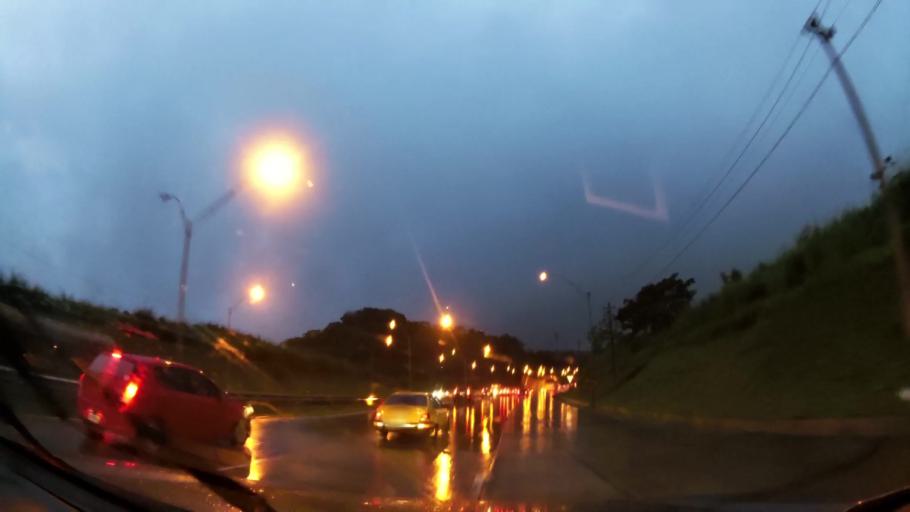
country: PA
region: Panama
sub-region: Distrito de Panama
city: Paraiso
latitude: 9.0232
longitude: -79.6394
